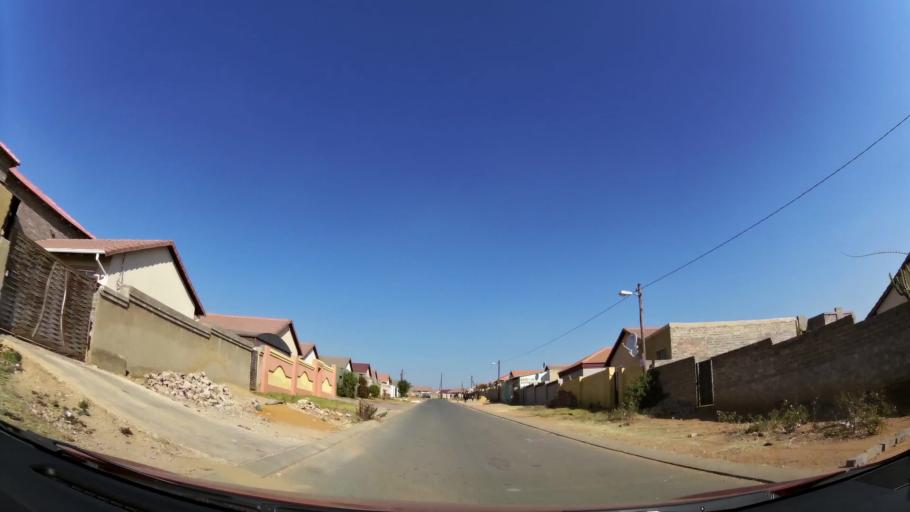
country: ZA
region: Gauteng
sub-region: West Rand District Municipality
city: Muldersdriseloop
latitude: -26.0370
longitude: 27.9267
